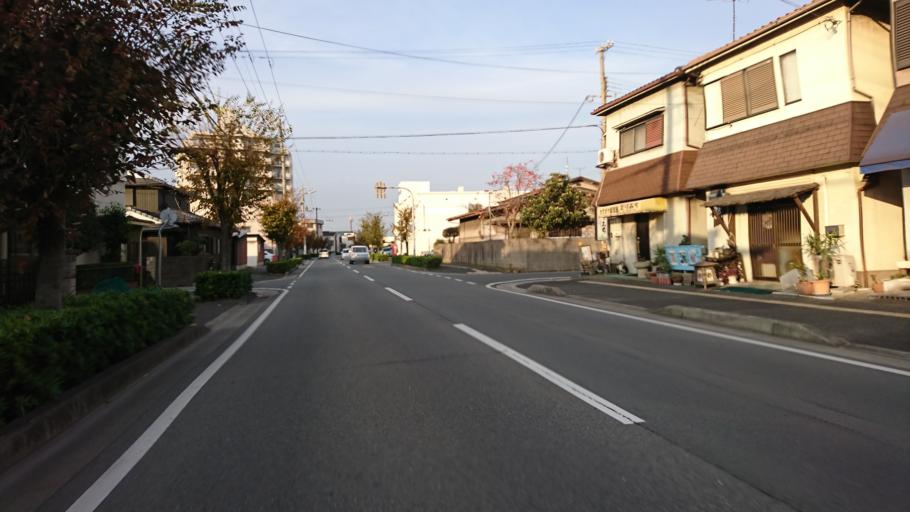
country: JP
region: Hyogo
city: Kakogawacho-honmachi
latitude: 34.7238
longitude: 134.8456
